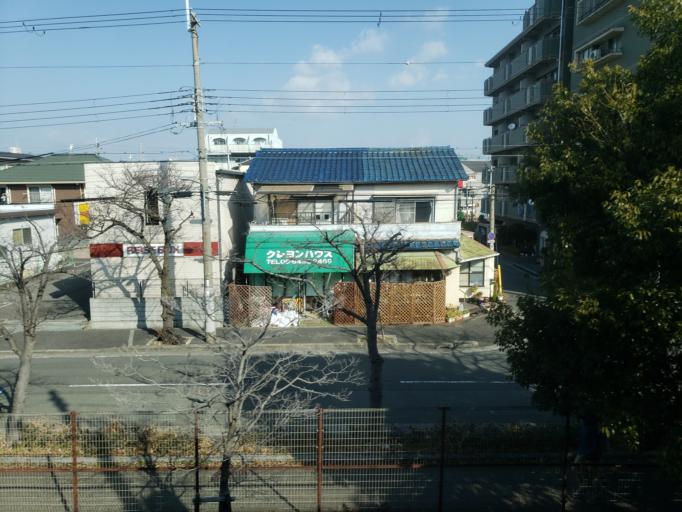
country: JP
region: Hyogo
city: Amagasaki
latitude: 34.7392
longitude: 135.3903
